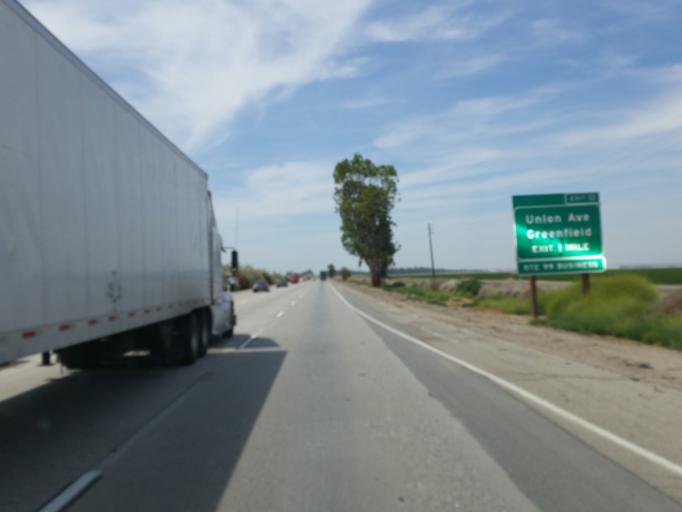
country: US
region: California
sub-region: Kern County
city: Greenfield
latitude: 35.1513
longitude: -118.9973
